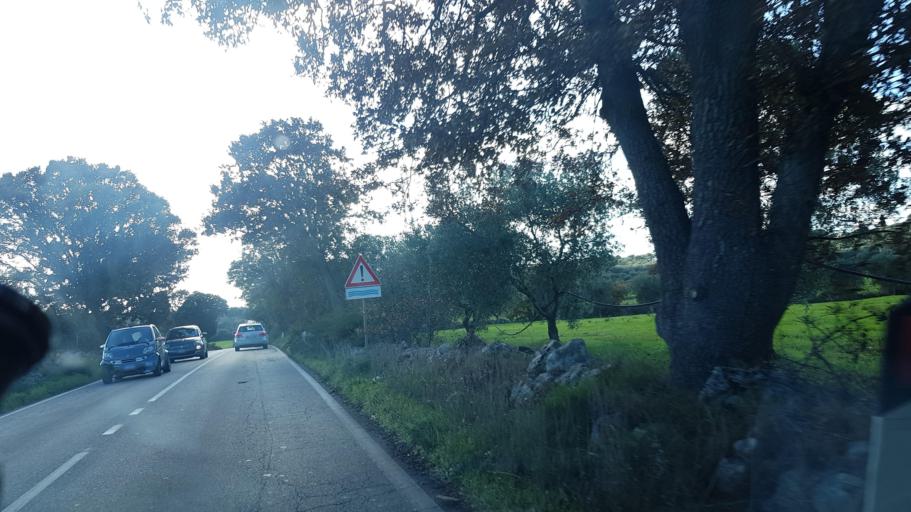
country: IT
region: Apulia
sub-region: Provincia di Brindisi
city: Ostuni
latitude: 40.6978
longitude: 17.5590
